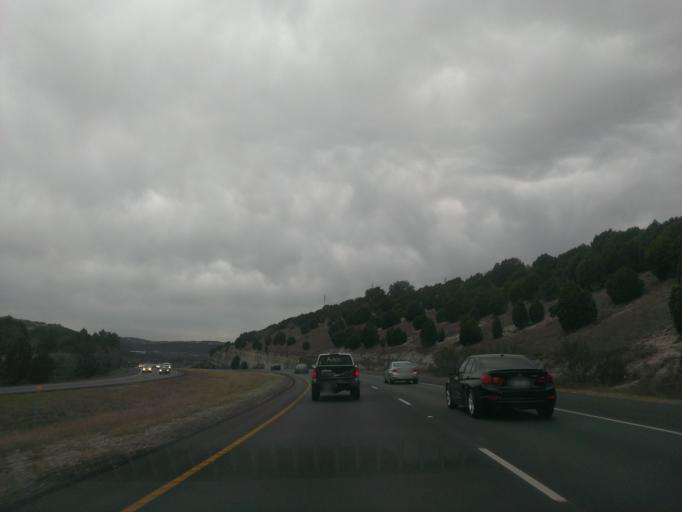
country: US
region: Texas
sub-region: Williamson County
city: Jollyville
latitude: 30.3880
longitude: -97.7621
